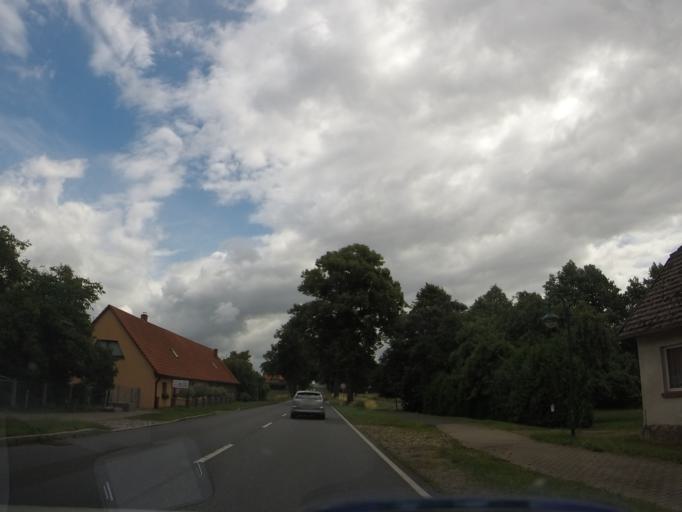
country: DE
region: Mecklenburg-Vorpommern
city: Lalendorf
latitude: 53.7660
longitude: 12.3436
